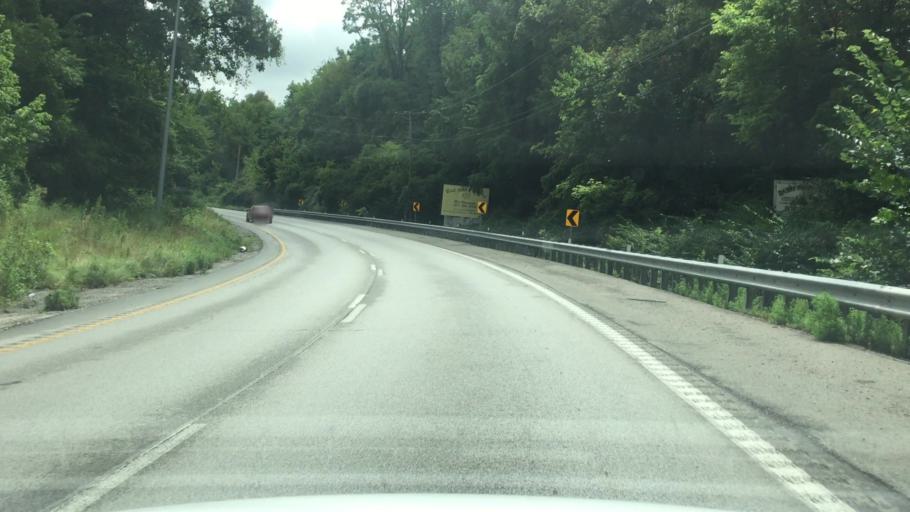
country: US
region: Missouri
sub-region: Jackson County
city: Lees Summit
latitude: 38.9538
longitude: -94.4208
